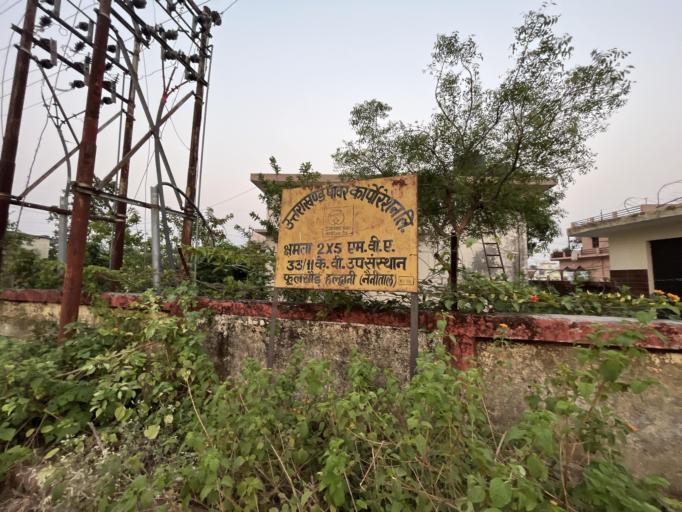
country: IN
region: Uttarakhand
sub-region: Naini Tal
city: Haldwani
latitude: 29.1828
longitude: 79.4869
